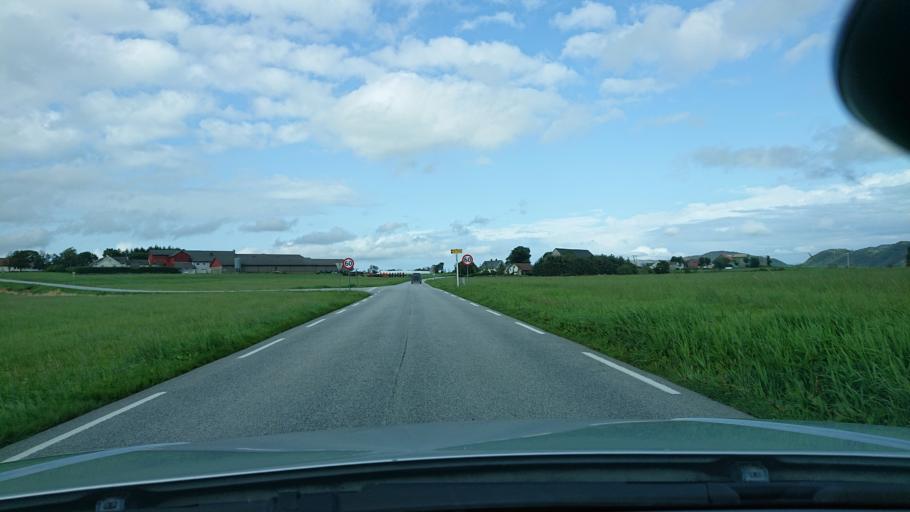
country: NO
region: Rogaland
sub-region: Gjesdal
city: Algard
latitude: 58.6892
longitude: 5.7687
